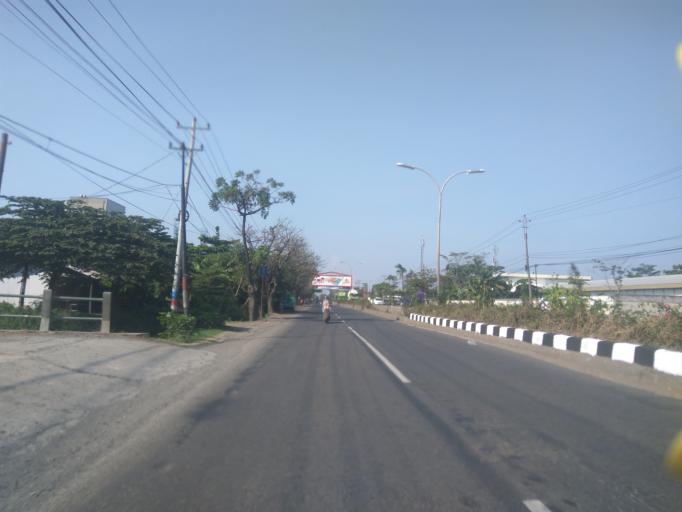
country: ID
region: Central Java
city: Semarang
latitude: -6.9484
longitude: 110.4886
